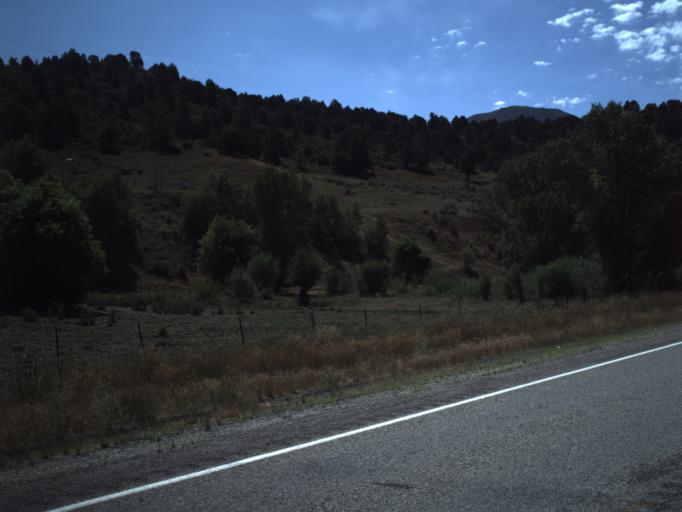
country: US
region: Utah
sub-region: Utah County
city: Woodland Hills
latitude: 39.9823
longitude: -111.5026
